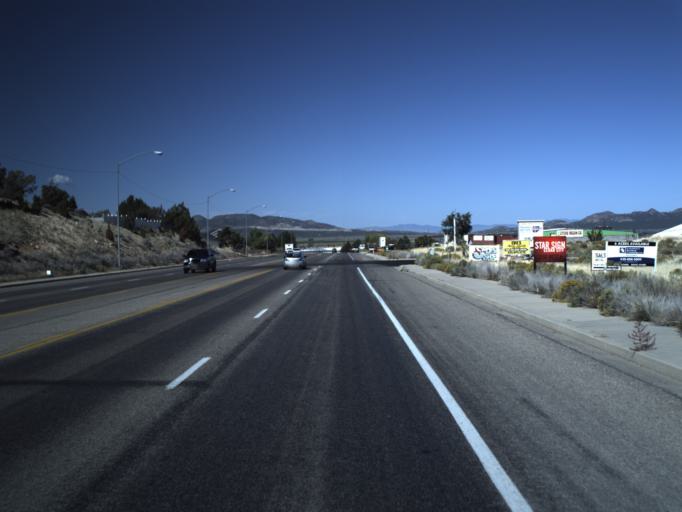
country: US
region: Utah
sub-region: Iron County
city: Cedar City
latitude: 37.6823
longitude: -113.0890
